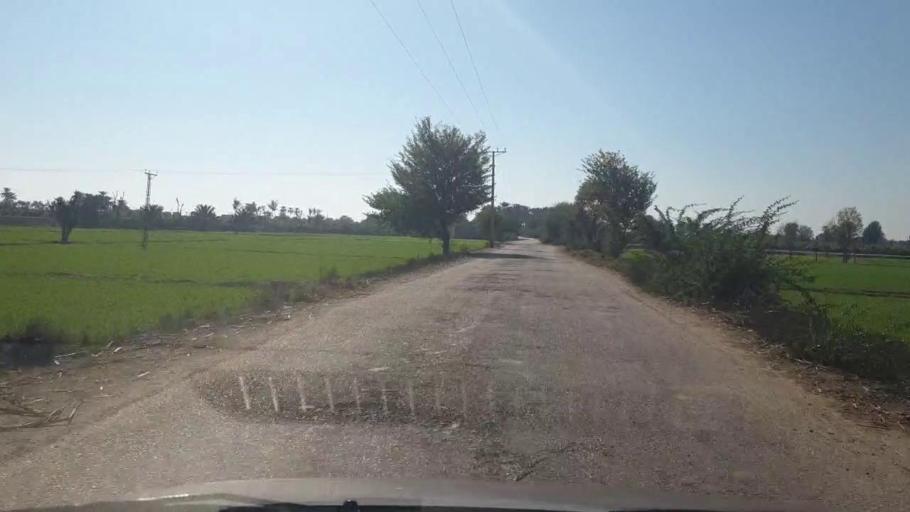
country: PK
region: Sindh
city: Bozdar
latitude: 27.2512
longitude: 68.6520
